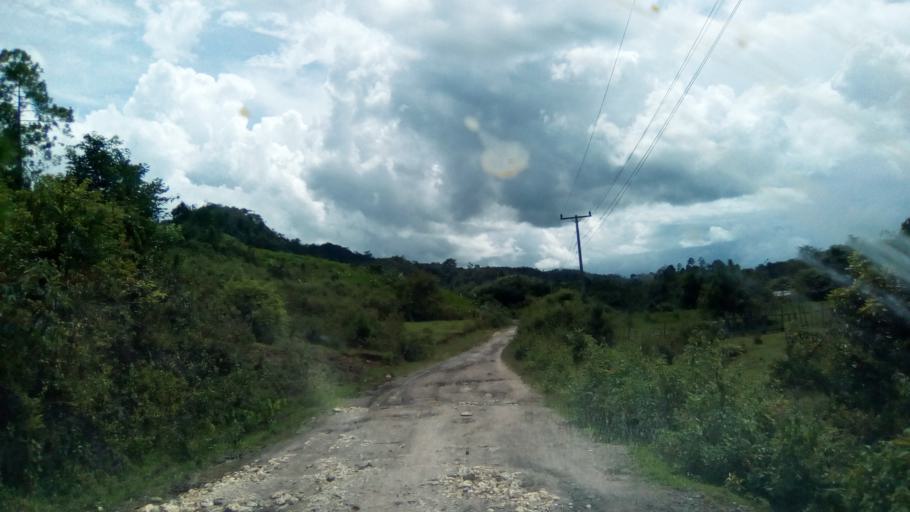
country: LA
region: Xiangkhoang
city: Muang Phonsavan
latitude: 19.3402
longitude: 103.6211
